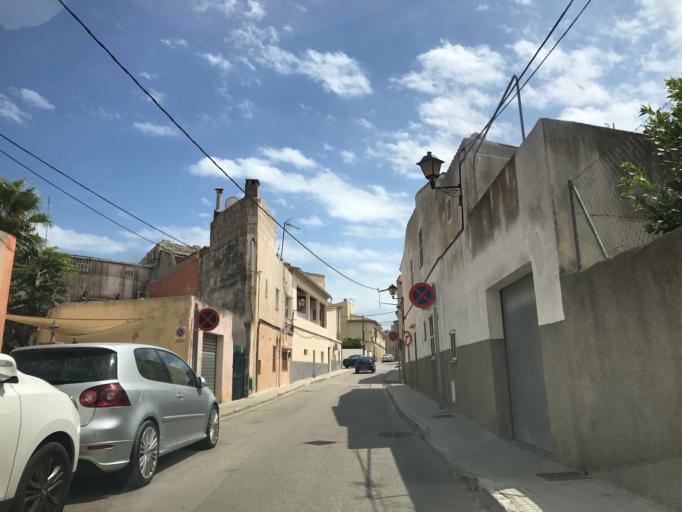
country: ES
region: Balearic Islands
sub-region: Illes Balears
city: Son Servera
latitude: 39.6255
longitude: 3.3568
